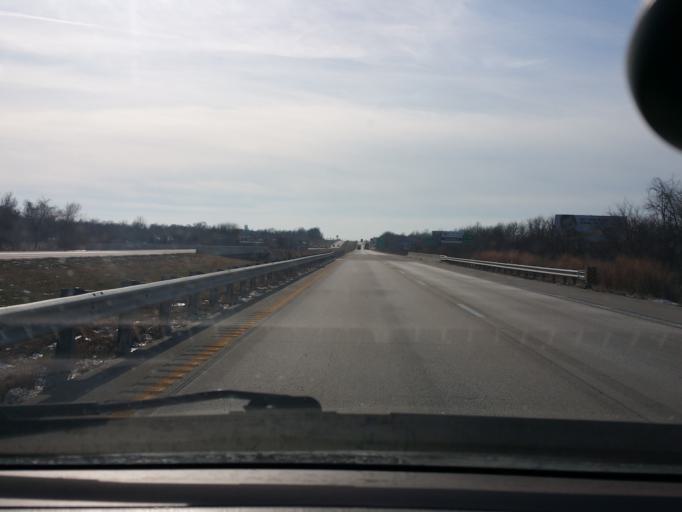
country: US
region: Missouri
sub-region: Clay County
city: Kearney
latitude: 39.3898
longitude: -94.3606
